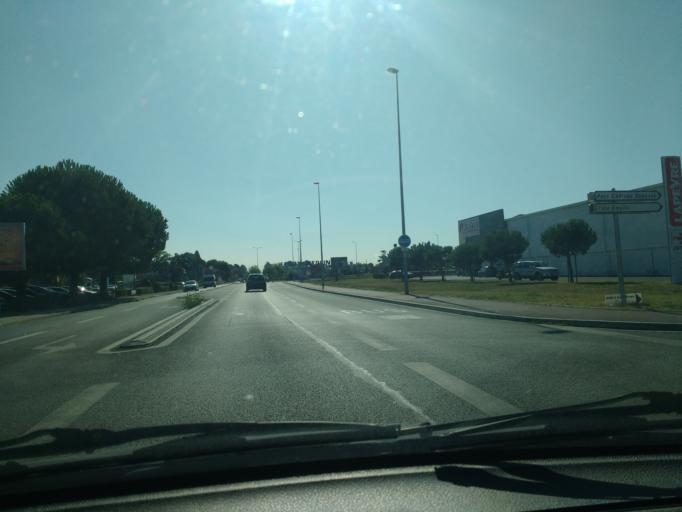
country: FR
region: Aquitaine
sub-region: Departement de la Gironde
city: Merignac
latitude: 44.8342
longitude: -0.6699
